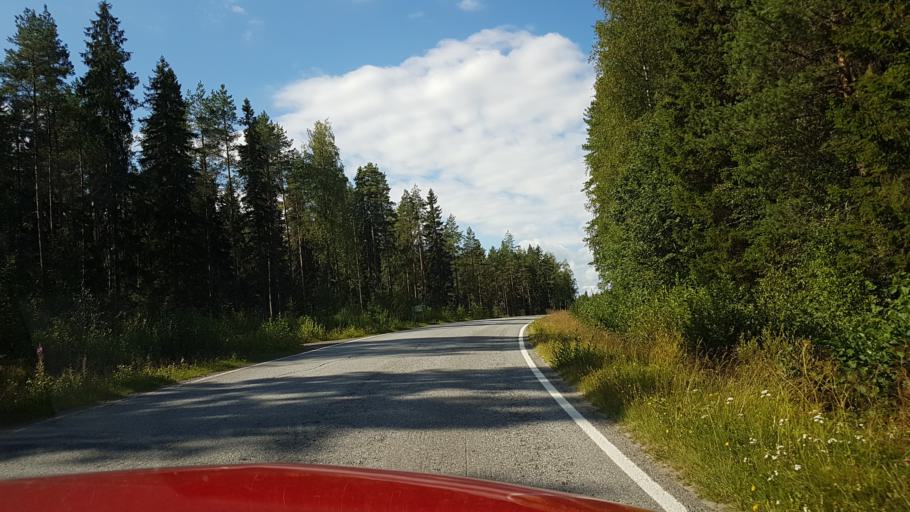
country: FI
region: Northern Ostrobothnia
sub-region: Ylivieska
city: Himanka
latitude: 64.0900
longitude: 23.7613
